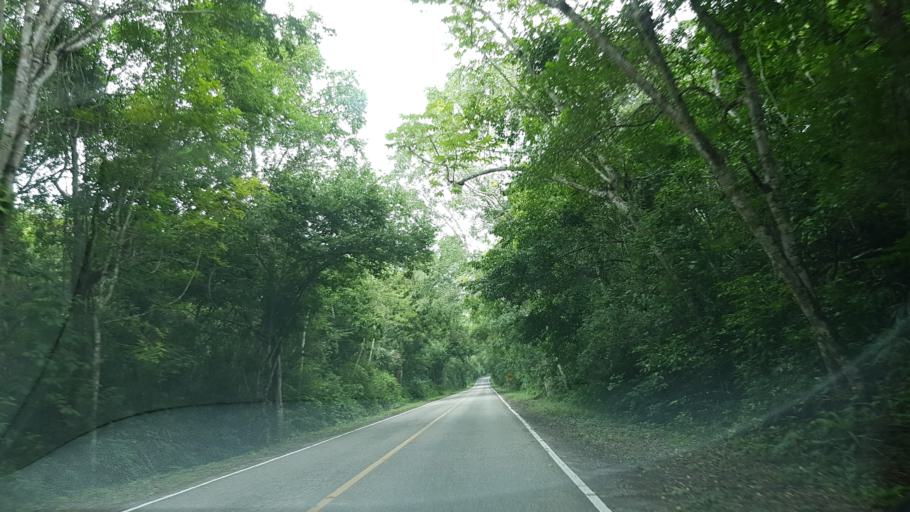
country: GT
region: Peten
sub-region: Municipio de San Jose
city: San Jose
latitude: 17.1714
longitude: -89.6433
